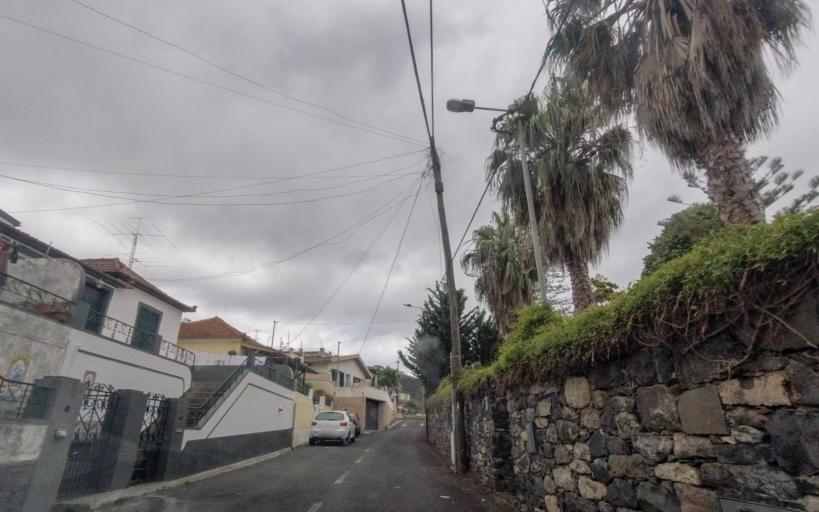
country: PT
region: Madeira
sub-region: Funchal
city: Nossa Senhora do Monte
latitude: 32.6580
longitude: -16.8818
